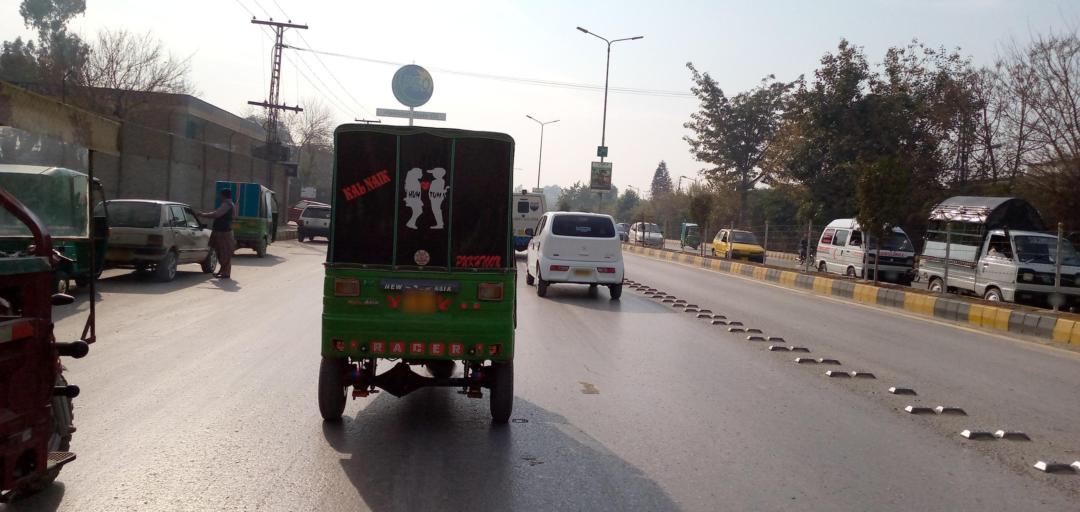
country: PK
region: Khyber Pakhtunkhwa
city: Peshawar
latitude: 34.0117
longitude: 71.5401
